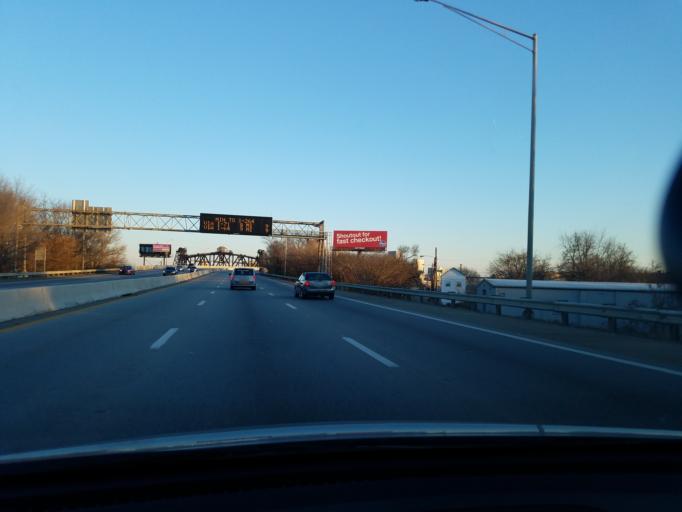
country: US
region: Kentucky
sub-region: Jefferson County
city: Louisville
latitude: 38.2653
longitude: -85.7770
